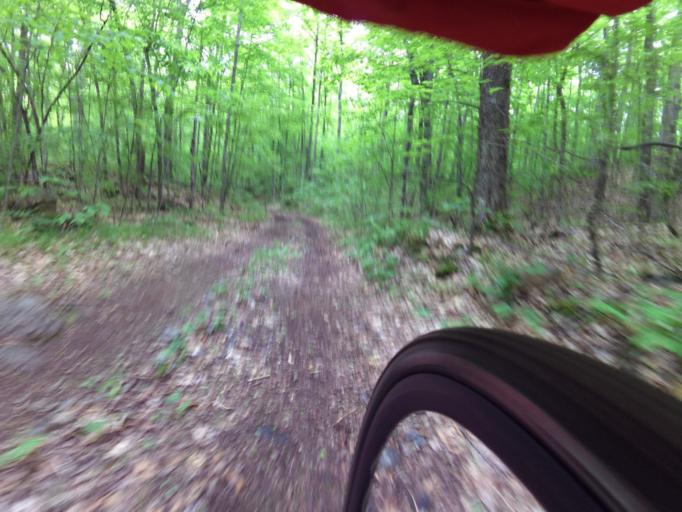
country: CA
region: Ontario
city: Arnprior
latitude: 45.1803
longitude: -76.5331
